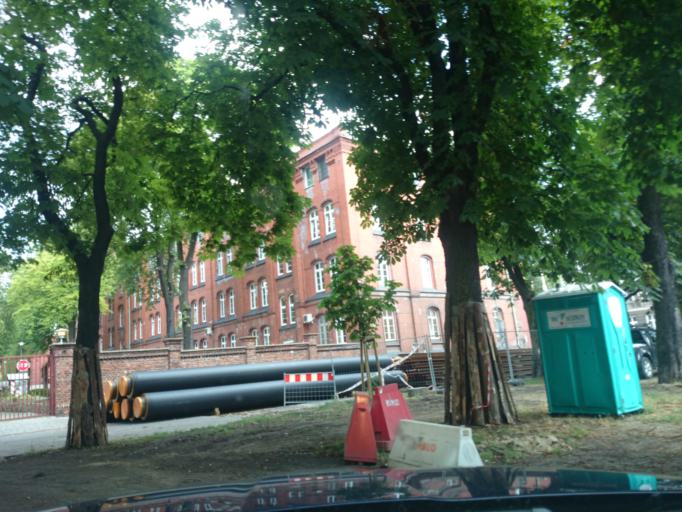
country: PL
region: West Pomeranian Voivodeship
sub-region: Szczecin
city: Szczecin
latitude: 53.4209
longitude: 14.5446
